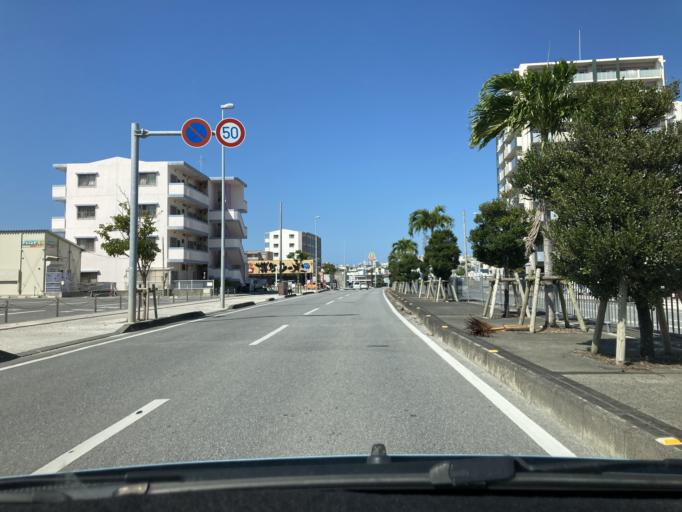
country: JP
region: Okinawa
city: Tomigusuku
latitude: 26.1906
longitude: 127.7156
